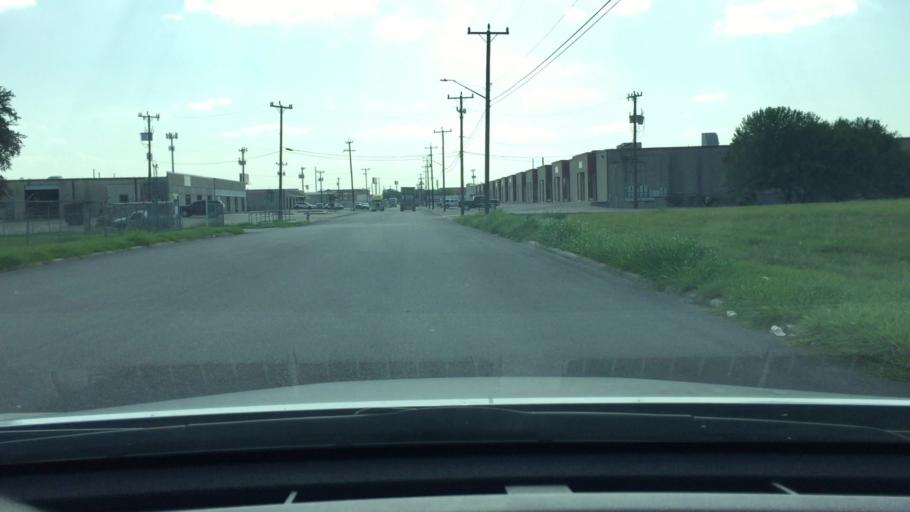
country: US
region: Texas
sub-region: Bexar County
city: Kirby
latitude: 29.4881
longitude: -98.3953
